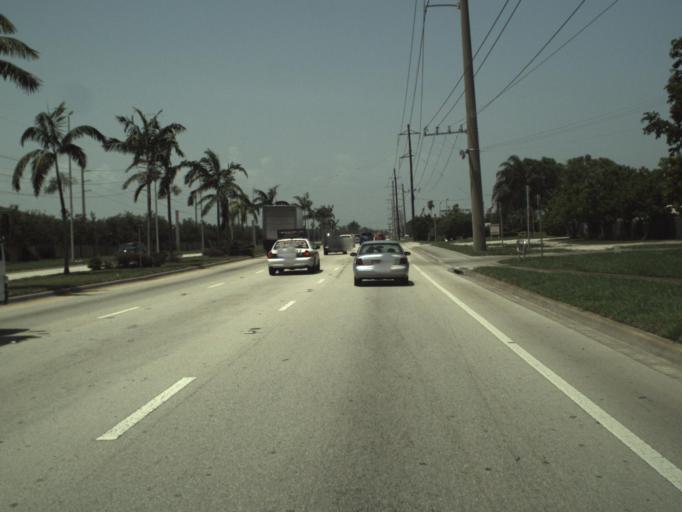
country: US
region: Florida
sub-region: Broward County
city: Tedder
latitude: 26.2813
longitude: -80.1522
